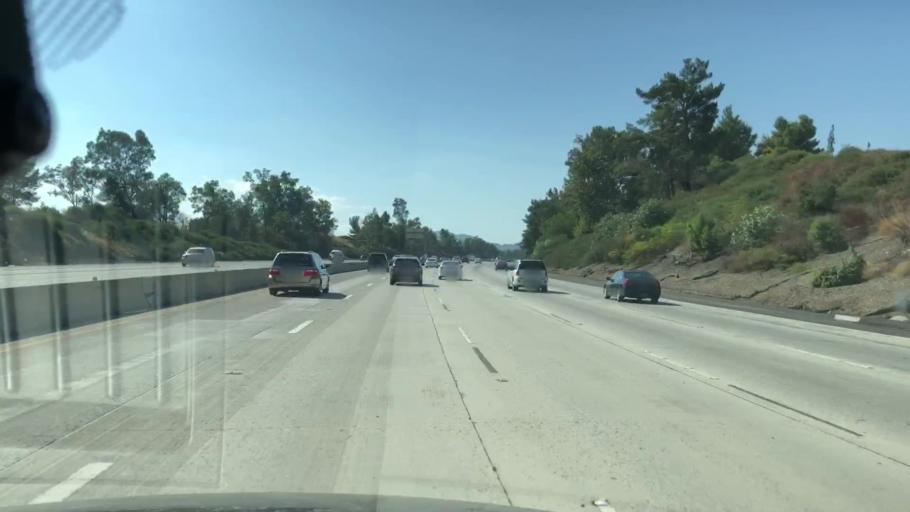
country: US
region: California
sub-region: Los Angeles County
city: Northridge
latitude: 34.2750
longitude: -118.5370
